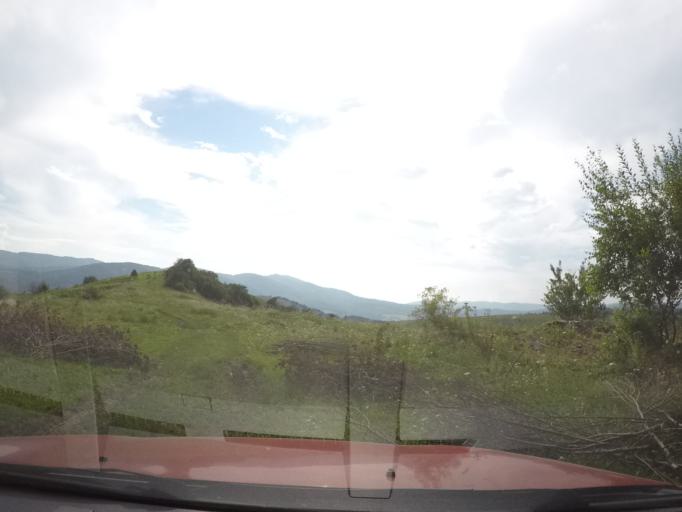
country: PL
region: Subcarpathian Voivodeship
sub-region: Powiat bieszczadzki
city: Lutowiska
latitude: 49.0316
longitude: 22.6454
